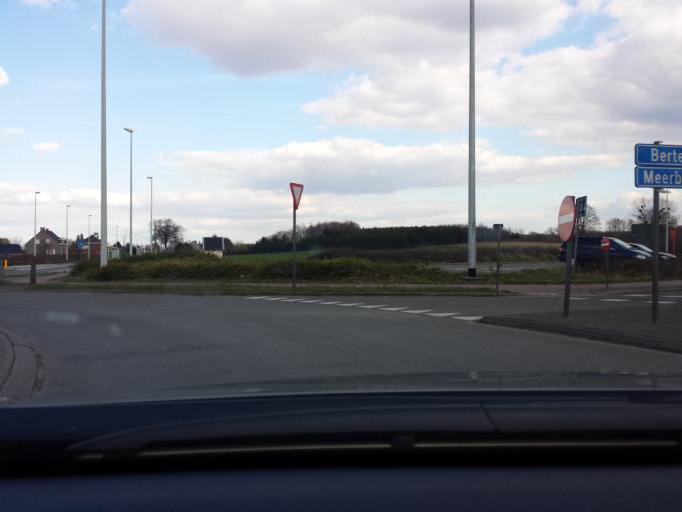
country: BE
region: Flanders
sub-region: Provincie Vlaams-Brabant
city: Kortenberg
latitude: 50.8914
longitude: 4.5706
